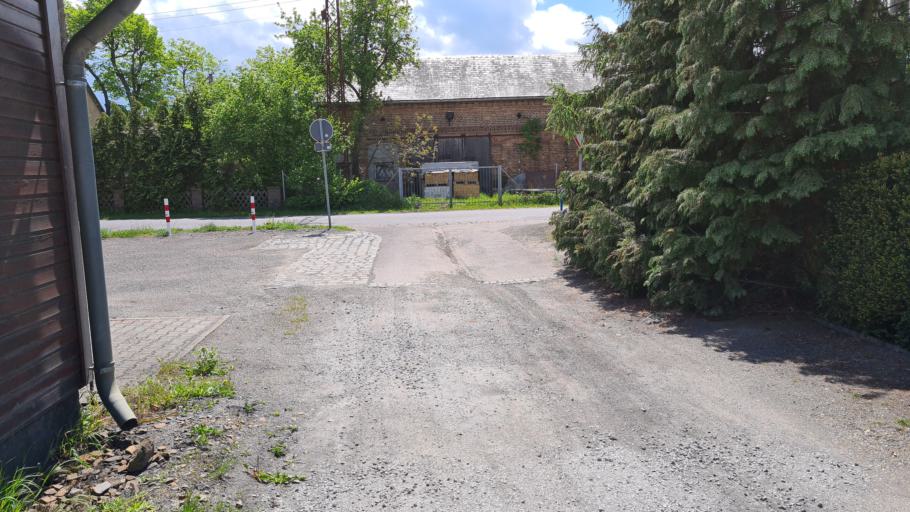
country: DE
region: Brandenburg
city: Grossraschen
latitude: 51.5883
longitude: 14.0340
